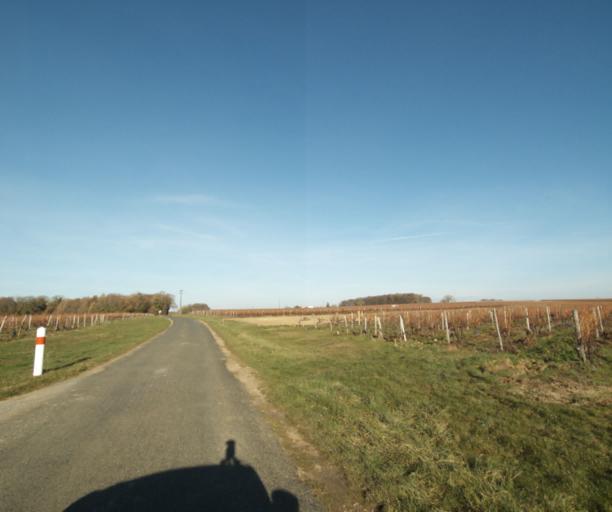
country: FR
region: Poitou-Charentes
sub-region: Departement de la Charente-Maritime
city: Cherac
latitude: 45.7289
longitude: -0.4478
